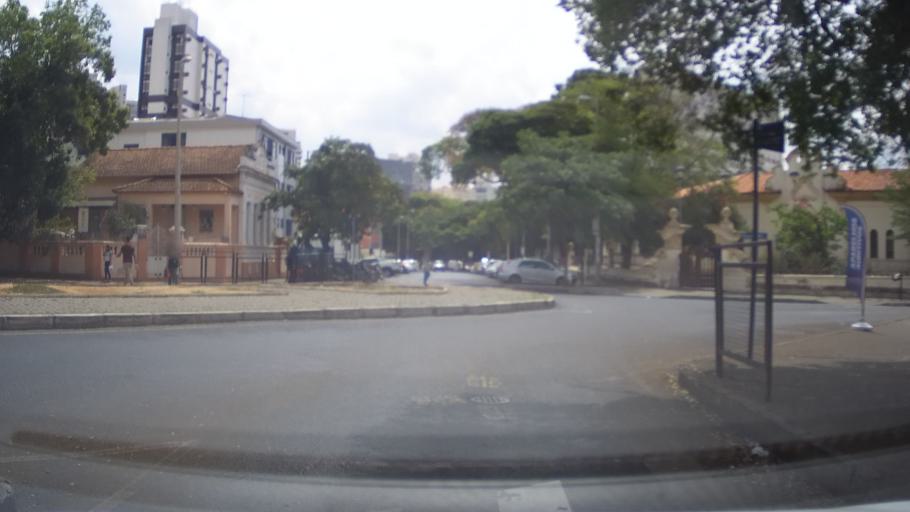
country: BR
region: Minas Gerais
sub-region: Belo Horizonte
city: Belo Horizonte
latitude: -19.9266
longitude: -43.9294
